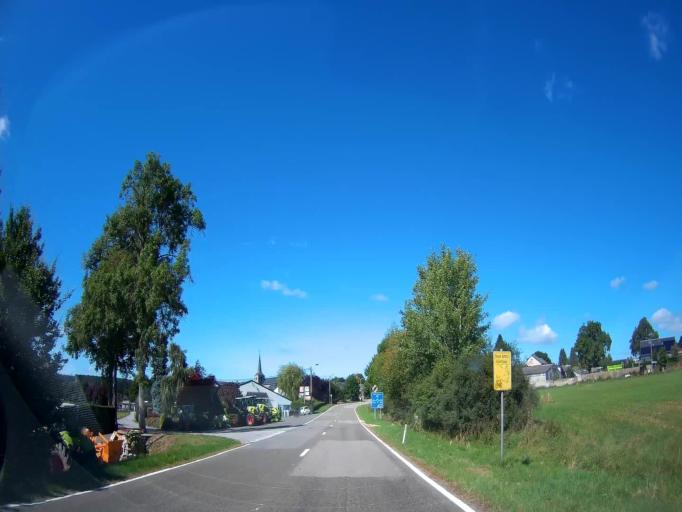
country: BE
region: Wallonia
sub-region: Province du Luxembourg
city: Bertogne
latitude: 50.1238
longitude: 5.6172
